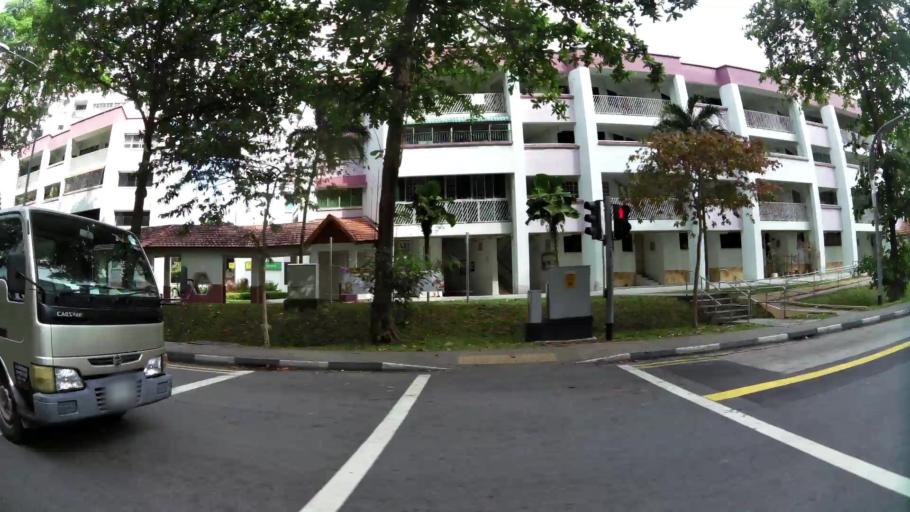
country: SG
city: Singapore
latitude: 1.3179
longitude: 103.8980
